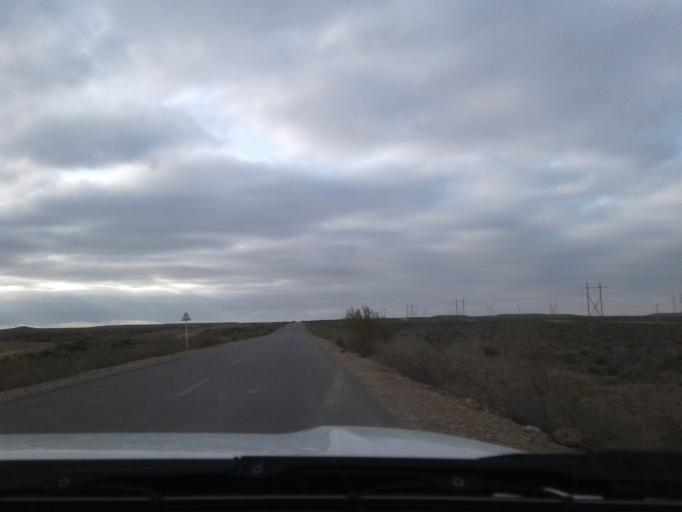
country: TM
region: Lebap
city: Sayat
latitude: 38.8372
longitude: 64.4672
